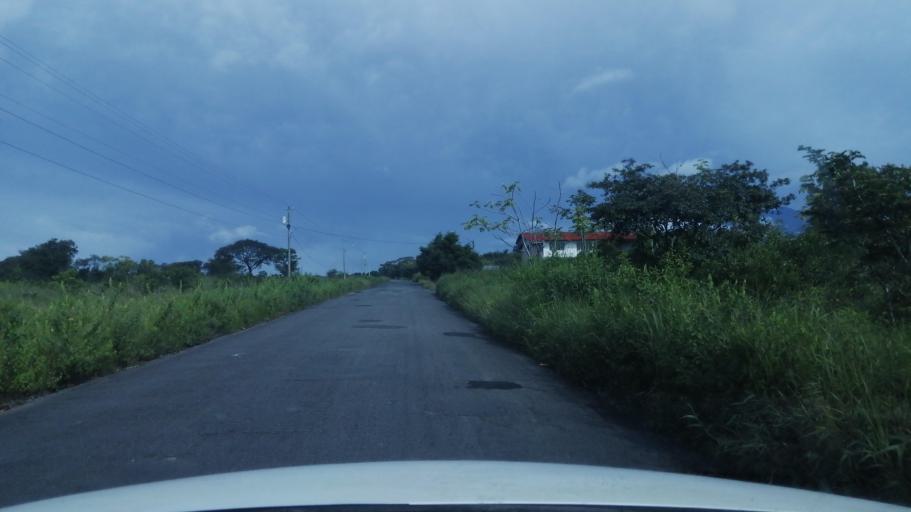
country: PA
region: Chiriqui
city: Potrerillos Abajo
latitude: 8.6697
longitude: -82.4328
